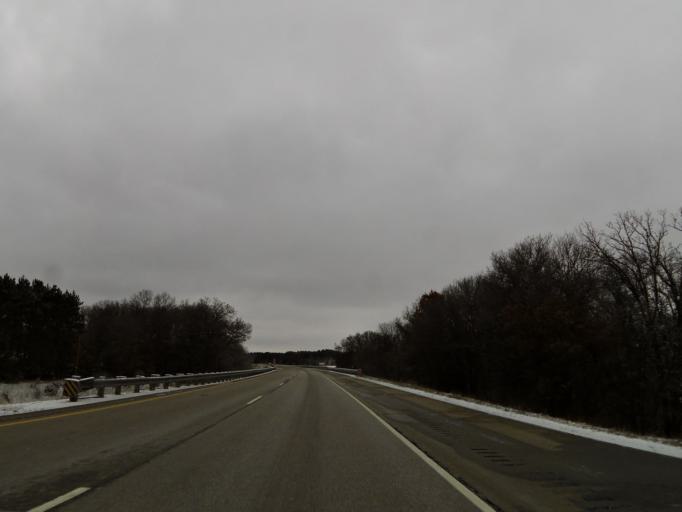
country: US
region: Wisconsin
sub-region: Trempealeau County
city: Osseo
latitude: 44.5453
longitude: -91.1607
